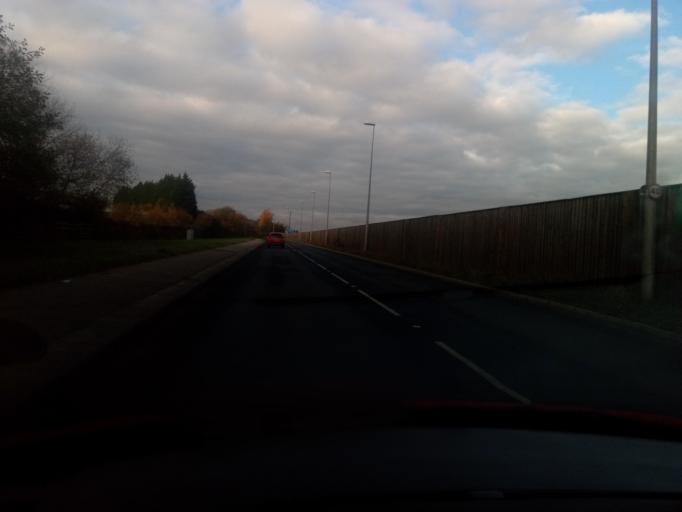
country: GB
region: England
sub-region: City and Borough of Leeds
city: Wetherby
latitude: 53.9351
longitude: -1.3749
